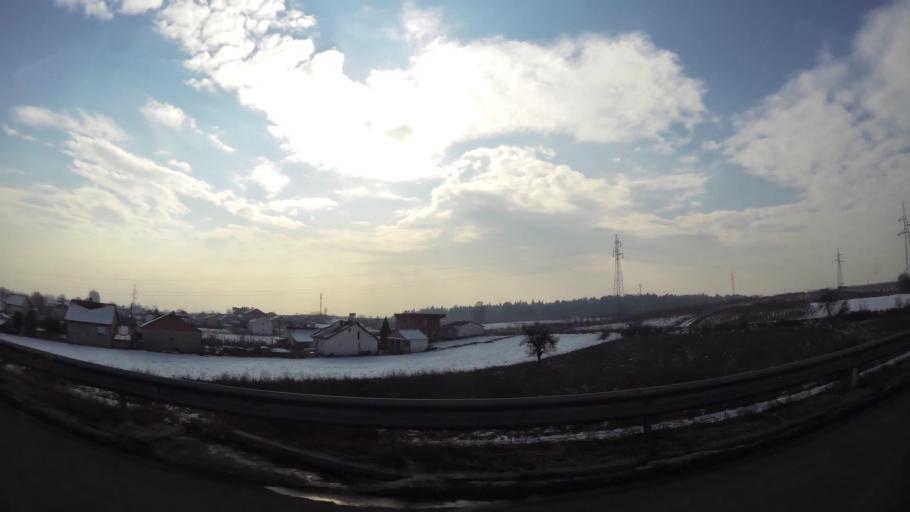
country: MK
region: Butel
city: Butel
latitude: 42.0454
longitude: 21.4416
